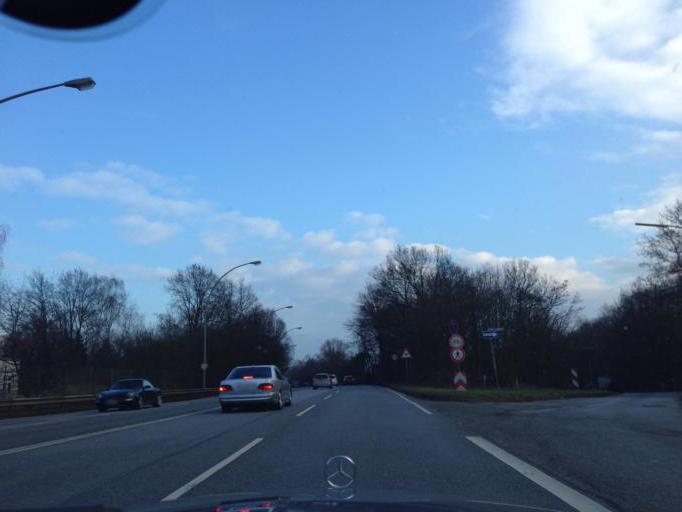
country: DE
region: Schleswig-Holstein
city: Oststeinbek
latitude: 53.5190
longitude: 10.1540
